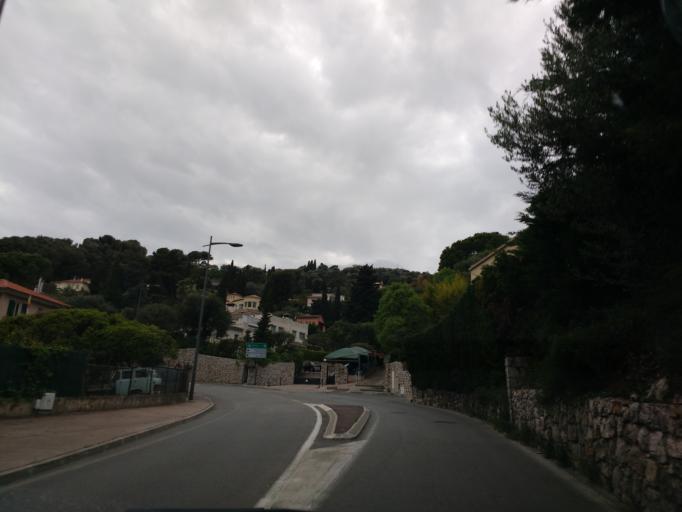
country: FR
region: Provence-Alpes-Cote d'Azur
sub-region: Departement des Alpes-Maritimes
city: Roquebrune-Cap-Martin
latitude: 43.7626
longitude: 7.4716
